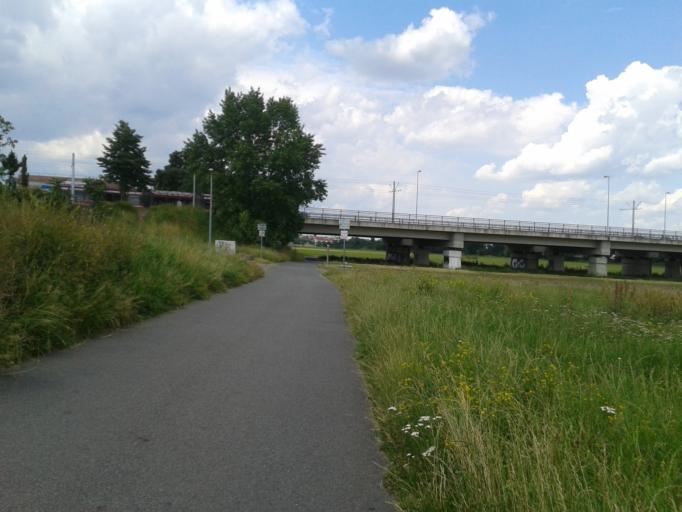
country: DE
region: Saxony
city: Dresden
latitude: 51.0652
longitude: 13.7173
